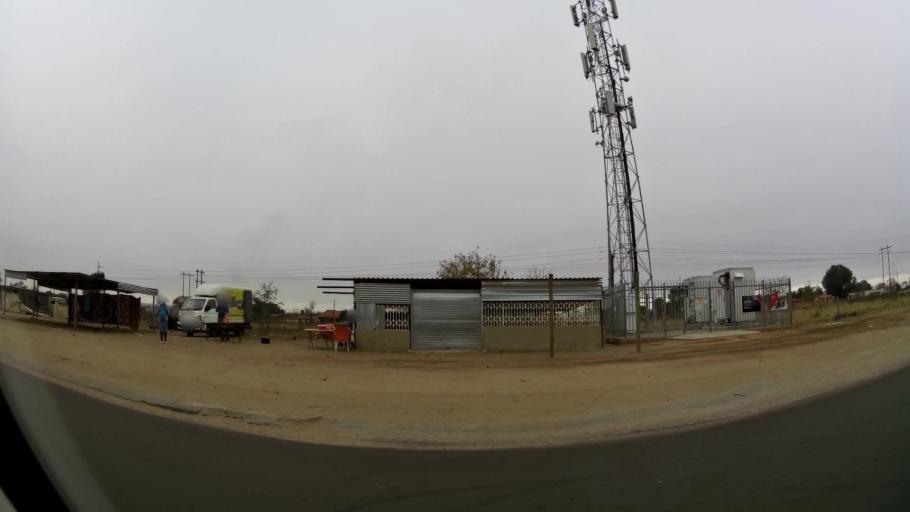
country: ZA
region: Limpopo
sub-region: Capricorn District Municipality
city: Polokwane
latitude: -23.8381
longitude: 29.3980
